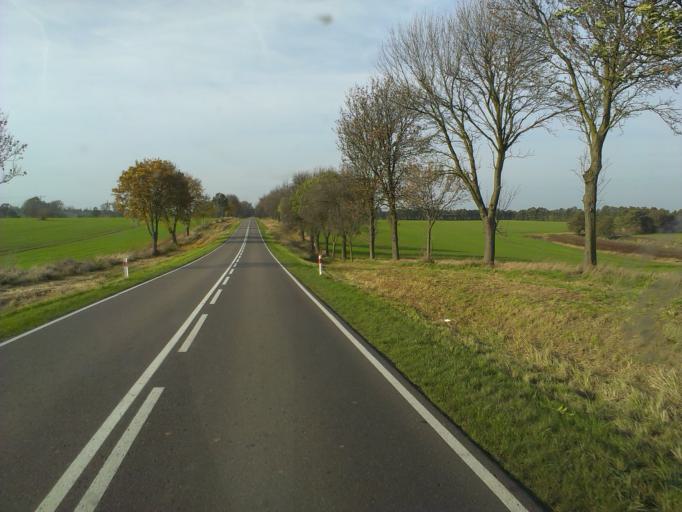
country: PL
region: West Pomeranian Voivodeship
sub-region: Powiat pyrzycki
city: Kozielice
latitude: 53.1225
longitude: 14.7817
